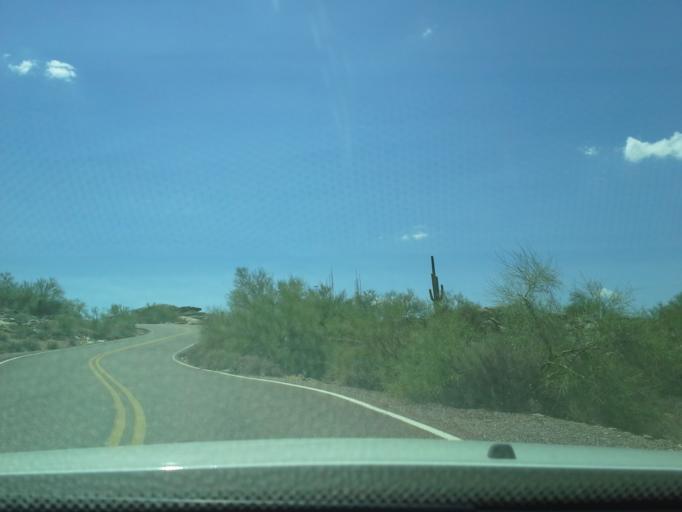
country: US
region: Arizona
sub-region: Maricopa County
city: Guadalupe
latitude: 33.3392
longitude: -112.0518
